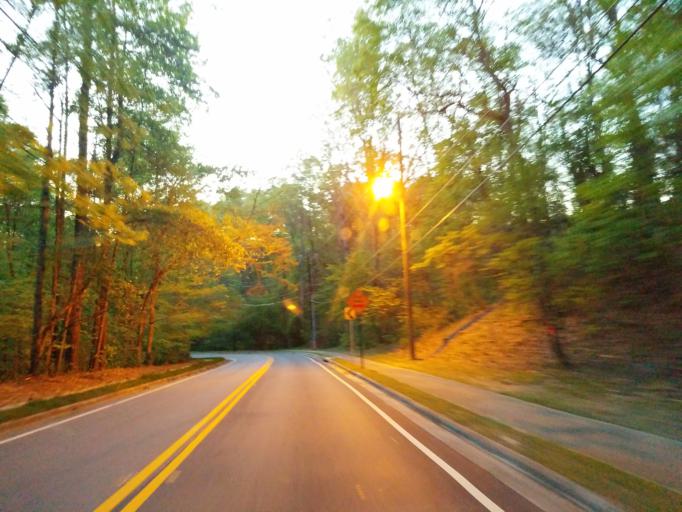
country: US
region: Georgia
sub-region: Fulton County
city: Sandy Springs
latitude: 33.9109
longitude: -84.4201
